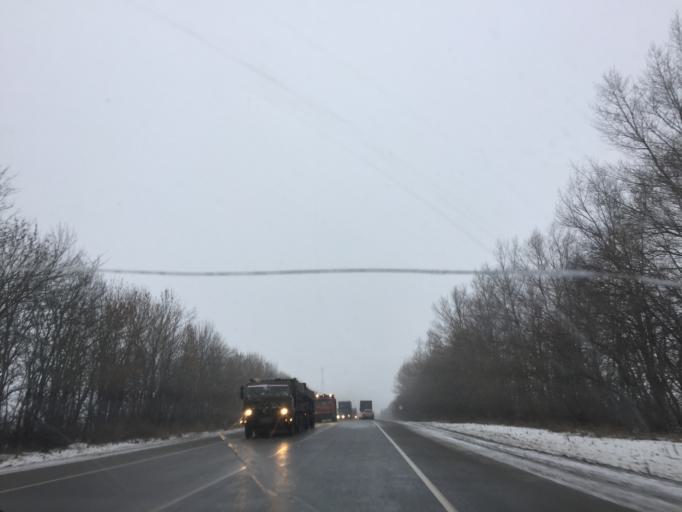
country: RU
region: Tula
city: Plavsk
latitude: 53.7898
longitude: 37.3684
